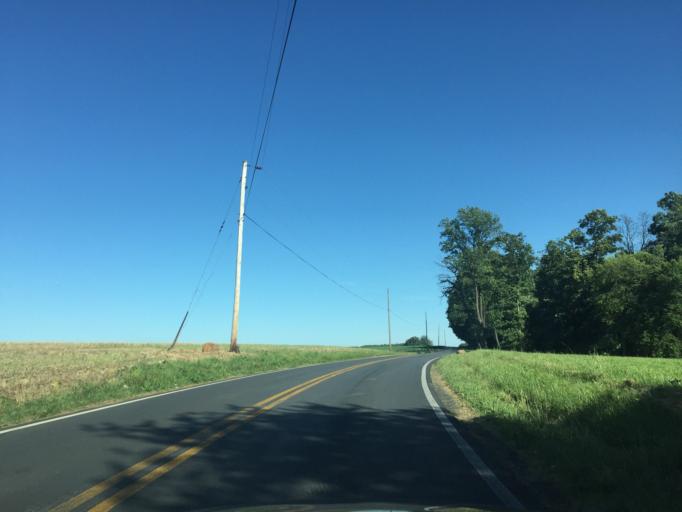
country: US
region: Maryland
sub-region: Carroll County
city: Westminster
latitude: 39.5780
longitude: -76.9208
